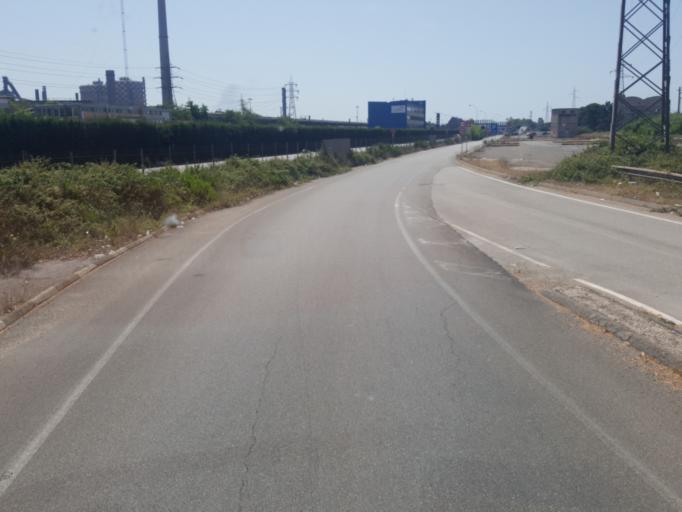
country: IT
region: Apulia
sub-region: Provincia di Taranto
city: Statte
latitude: 40.5034
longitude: 17.1981
